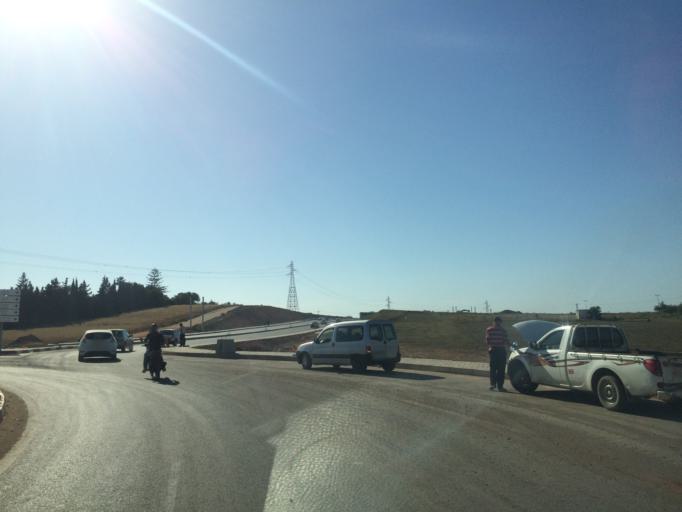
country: MA
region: Rabat-Sale-Zemmour-Zaer
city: Sale
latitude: 33.9786
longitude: -6.7382
